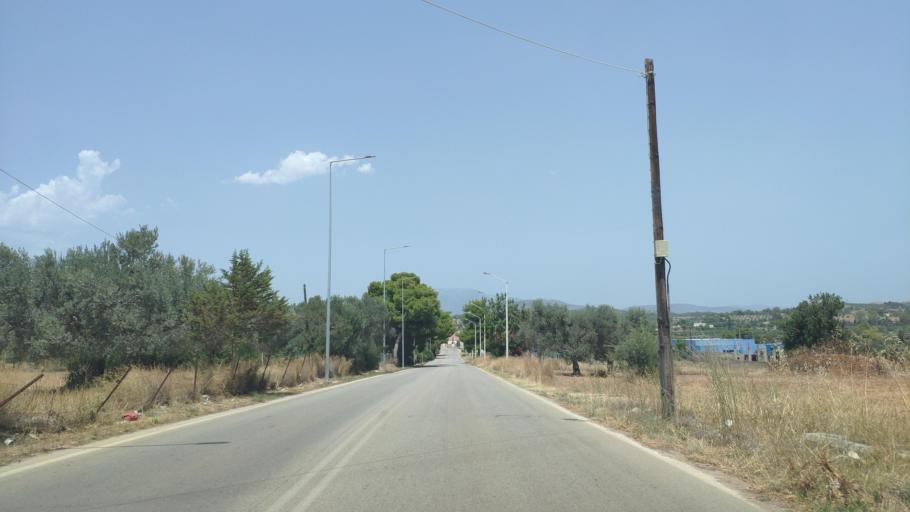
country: GR
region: Peloponnese
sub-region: Nomos Argolidos
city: Porto Cheli
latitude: 37.3395
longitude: 23.1563
